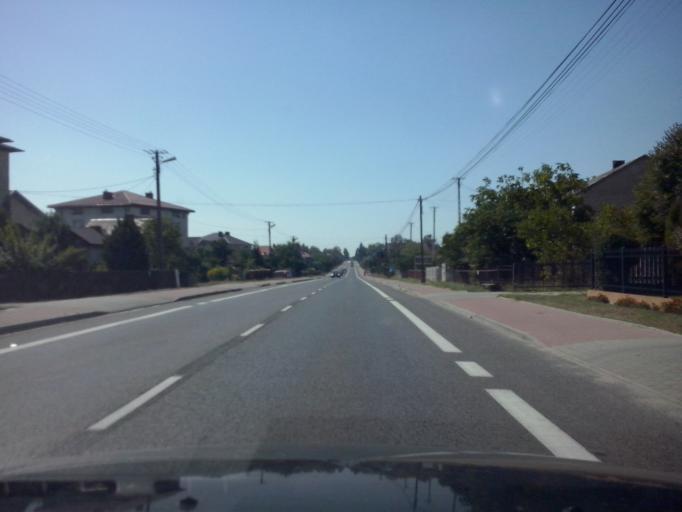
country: PL
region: Swietokrzyskie
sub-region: Powiat kielecki
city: Bieliny
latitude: 50.8494
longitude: 20.9292
